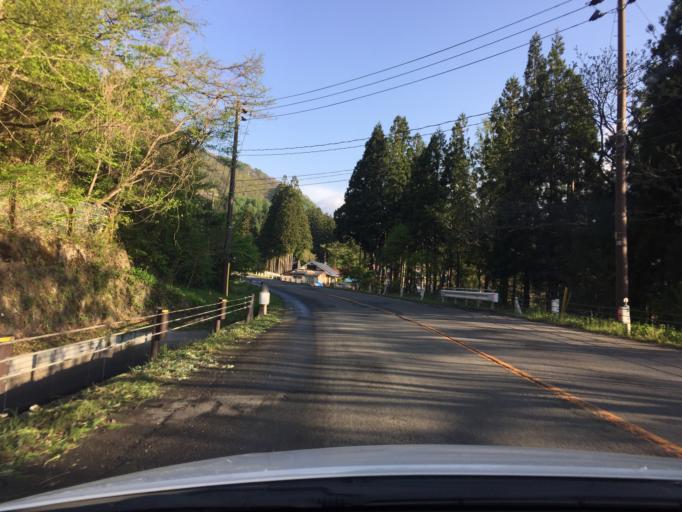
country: JP
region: Fukushima
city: Inawashiro
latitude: 37.6092
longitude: 140.1207
